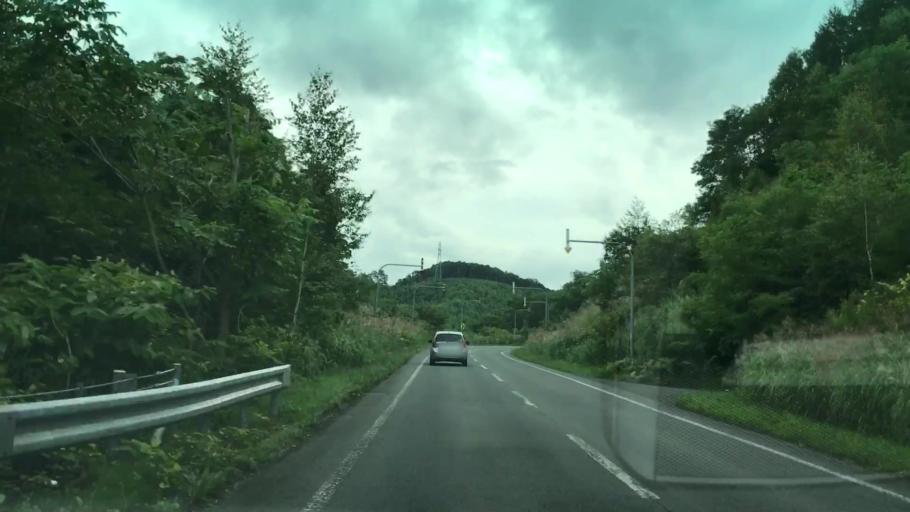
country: JP
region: Hokkaido
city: Yoichi
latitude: 43.1454
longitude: 140.8205
